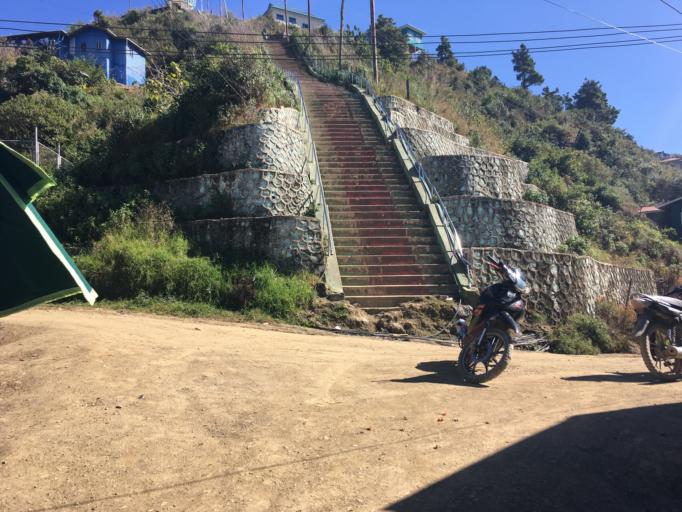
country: MM
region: Chin
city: Hakha
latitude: 22.6380
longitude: 93.6060
